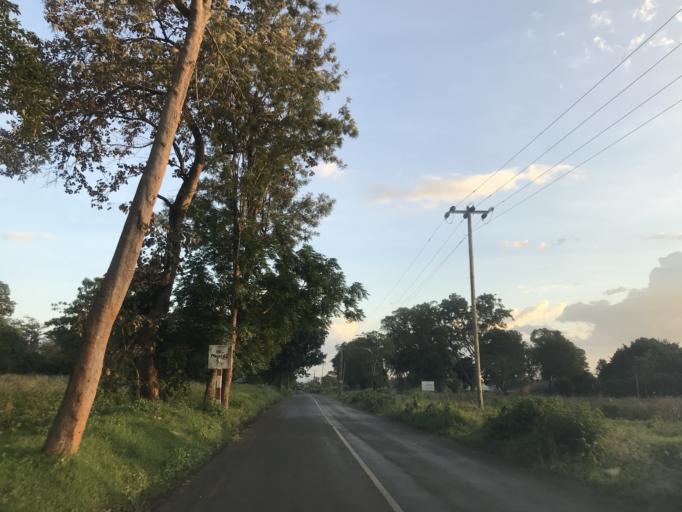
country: TZ
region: Arusha
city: Usa River
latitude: -3.3591
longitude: 36.8667
